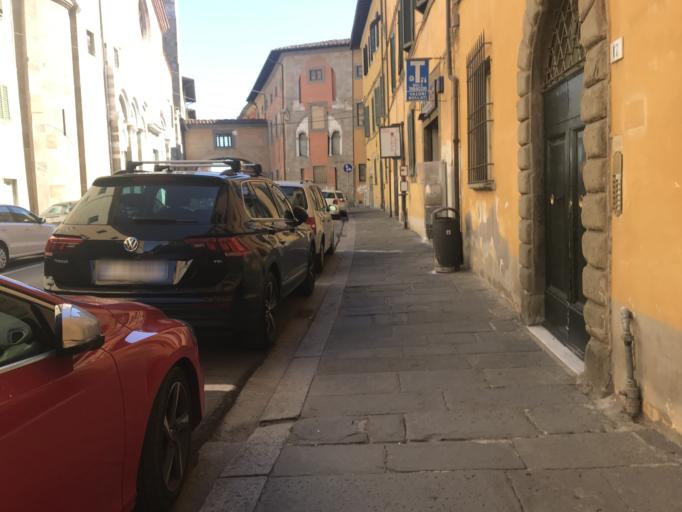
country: IT
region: Tuscany
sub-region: Province of Pisa
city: Pisa
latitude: 43.7172
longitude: 10.3964
